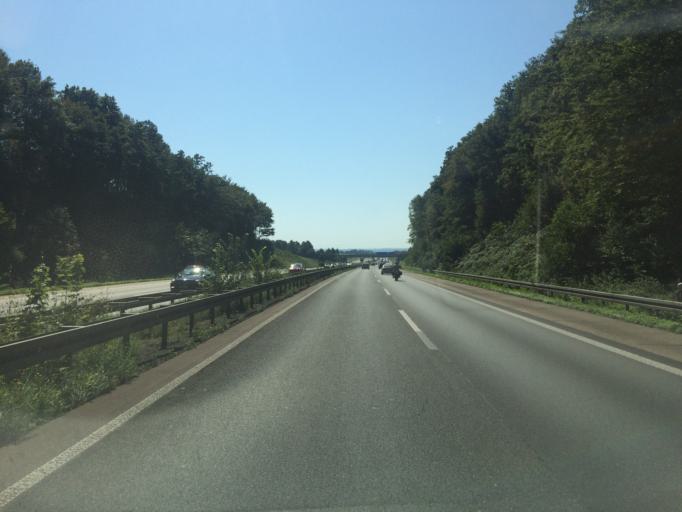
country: DE
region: North Rhine-Westphalia
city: Kamen
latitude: 51.6122
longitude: 7.6898
